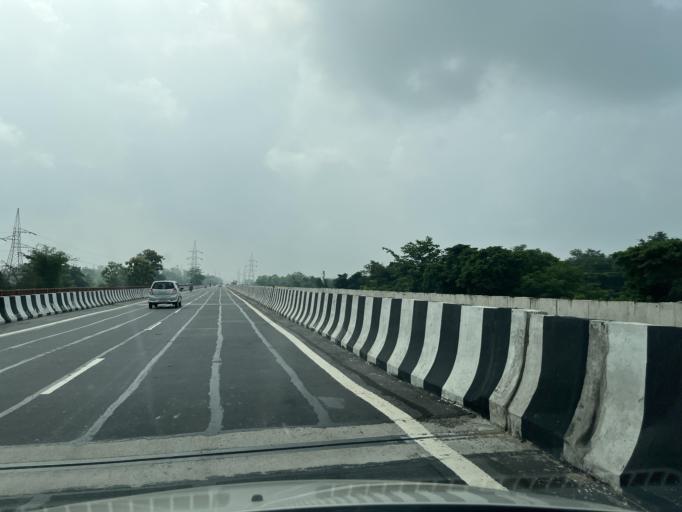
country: IN
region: Uttarakhand
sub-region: Dehradun
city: Raiwala
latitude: 30.1009
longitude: 78.1776
